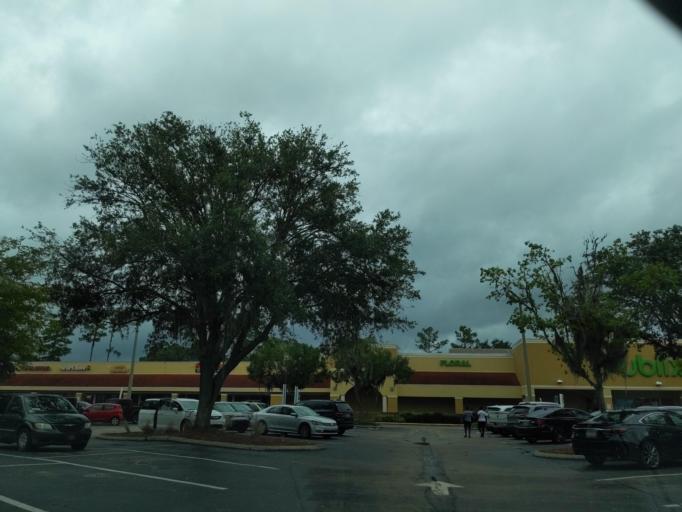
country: US
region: Florida
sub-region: Alachua County
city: Gainesville
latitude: 29.6010
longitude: -82.4208
